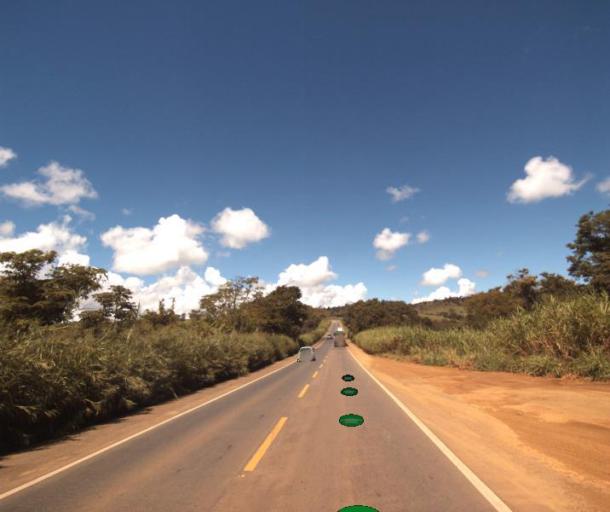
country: BR
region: Goias
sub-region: Anapolis
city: Anapolis
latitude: -16.1724
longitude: -49.0431
